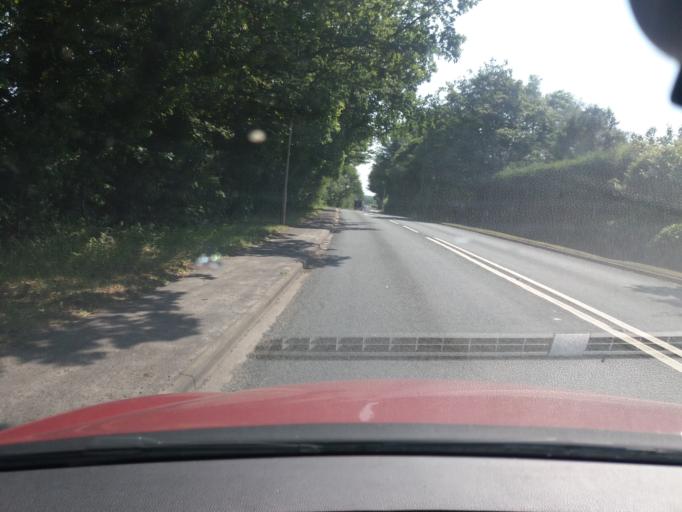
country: GB
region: England
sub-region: Lancashire
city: Euxton
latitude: 53.6445
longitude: -2.6782
